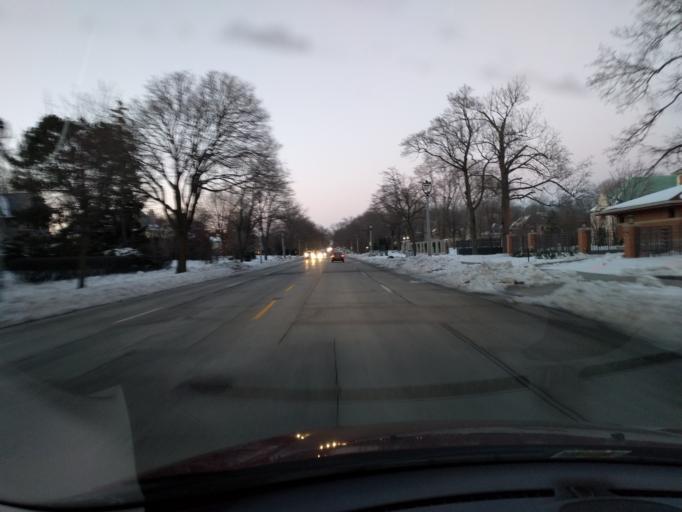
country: US
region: Wisconsin
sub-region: Milwaukee County
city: Shorewood
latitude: 43.0794
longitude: -87.8725
